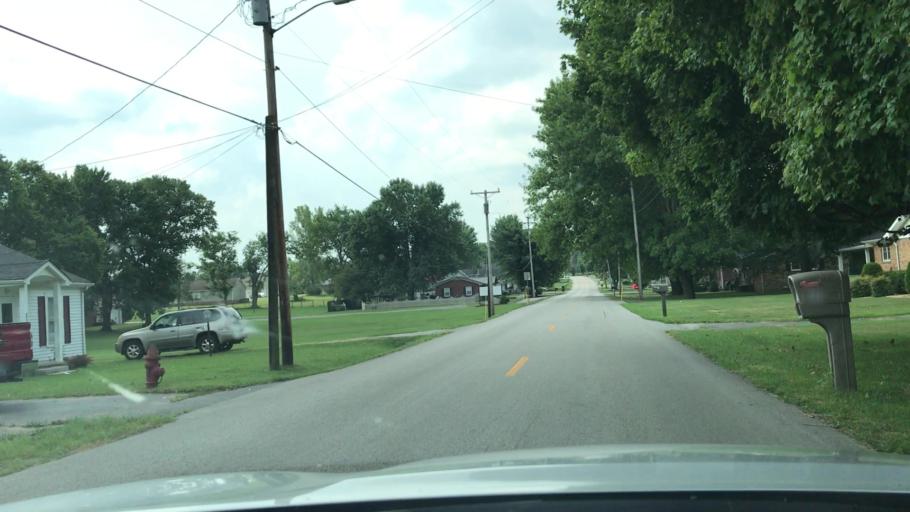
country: US
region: Kentucky
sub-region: Todd County
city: Elkton
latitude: 36.8066
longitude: -87.1481
